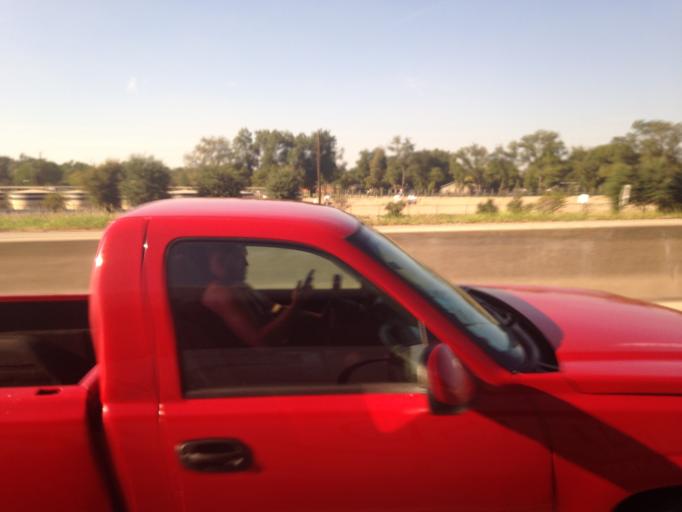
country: US
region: Texas
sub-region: Tarrant County
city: Haltom City
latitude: 32.7875
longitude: -97.2608
